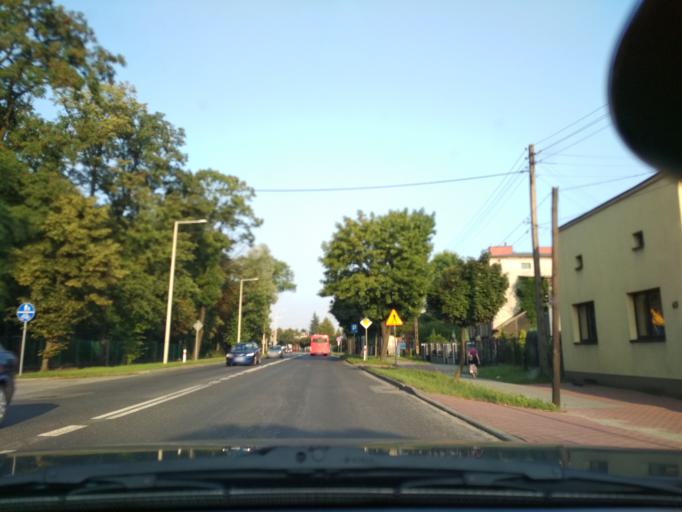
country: PL
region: Silesian Voivodeship
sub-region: Powiat zawiercianski
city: Zawiercie
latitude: 50.4794
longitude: 19.4441
